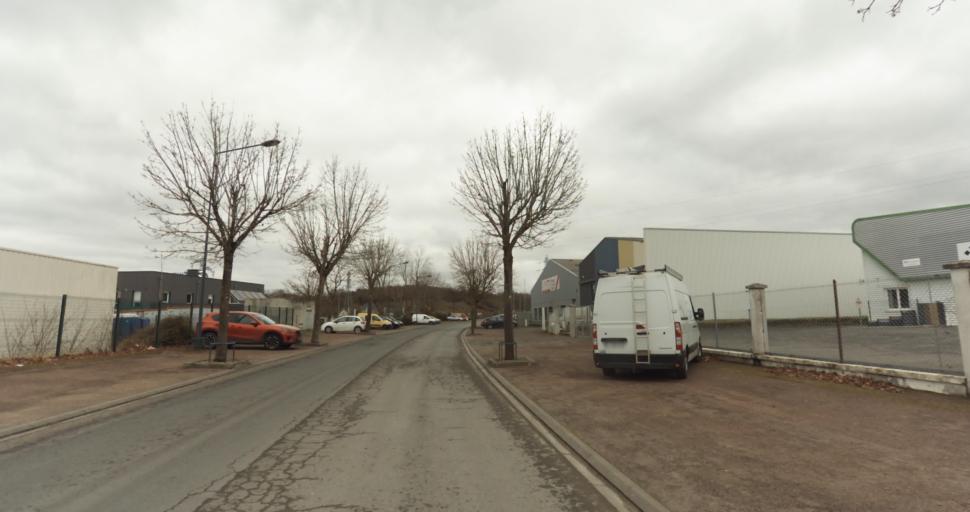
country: FR
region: Pays de la Loire
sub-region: Departement de Maine-et-Loire
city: Varrains
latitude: 47.2402
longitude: -0.0692
